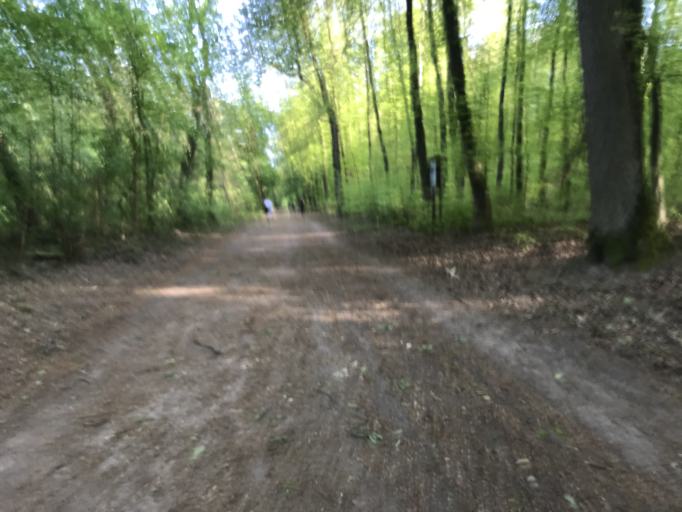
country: DE
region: Rheinland-Pfalz
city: Budenheim
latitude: 50.0116
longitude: 8.1845
